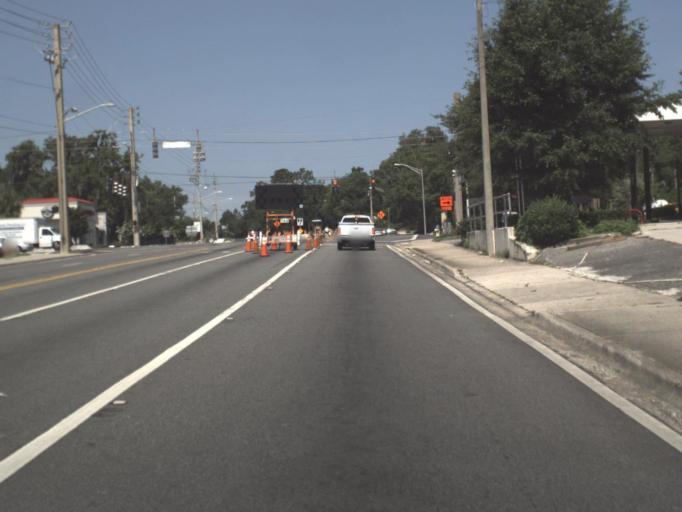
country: US
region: Florida
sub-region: Alachua County
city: Gainesville
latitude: 29.6365
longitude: -82.3385
